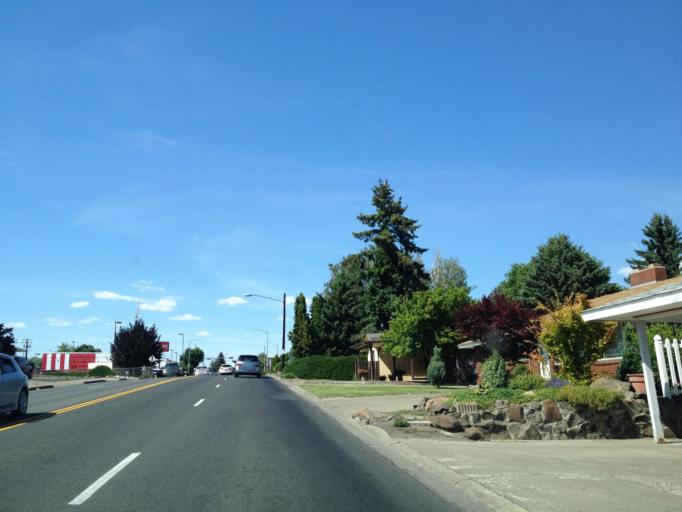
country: US
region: Washington
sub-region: Yakima County
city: West Valley
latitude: 46.5977
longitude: -120.5618
